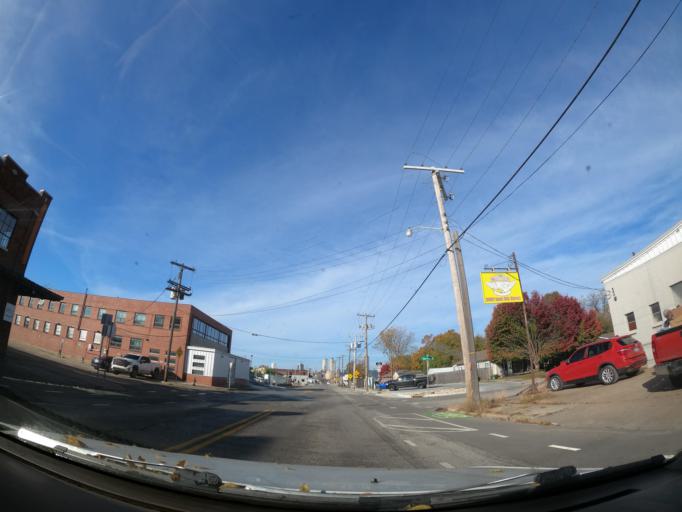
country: US
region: Oklahoma
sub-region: Tulsa County
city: Tulsa
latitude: 36.1521
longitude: -95.9634
